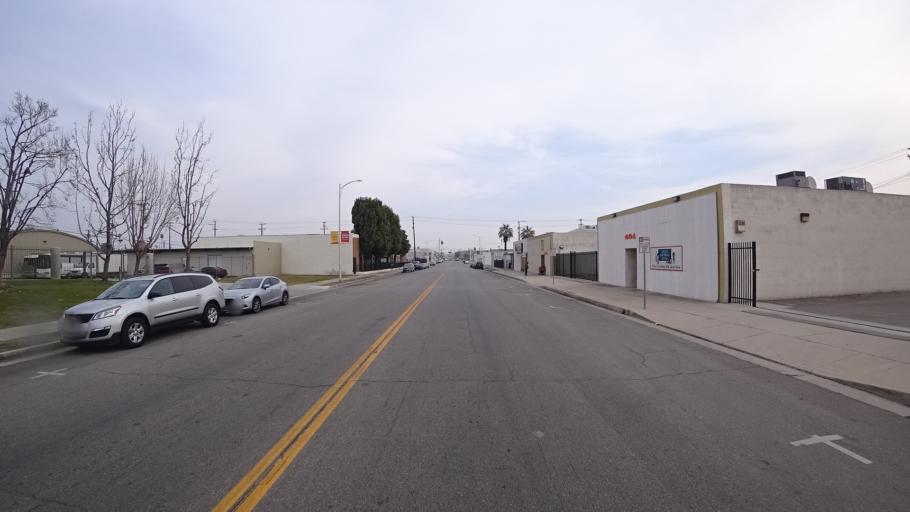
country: US
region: California
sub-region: Kern County
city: Bakersfield
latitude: 35.3762
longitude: -119.0062
